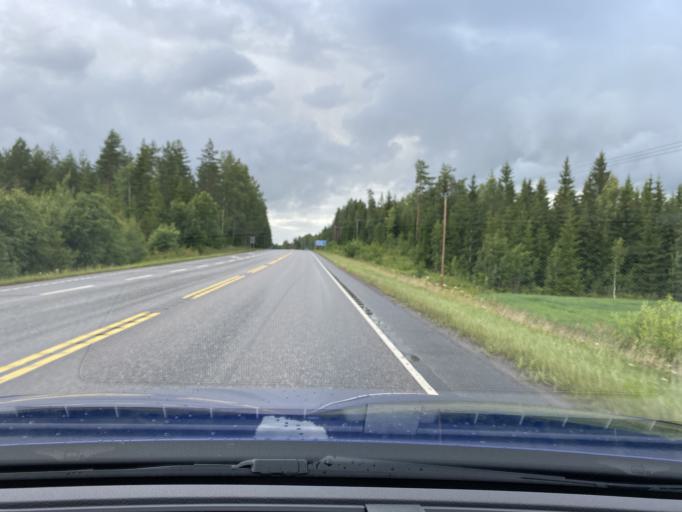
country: FI
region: Uusimaa
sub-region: Helsinki
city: Hyvinge
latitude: 60.5580
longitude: 24.8206
